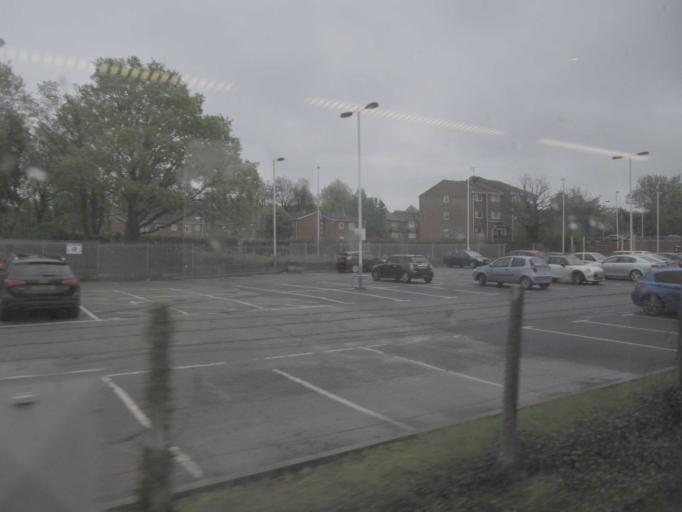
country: GB
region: England
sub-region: Wokingham
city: Wokingham
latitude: 51.4125
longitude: -0.8433
